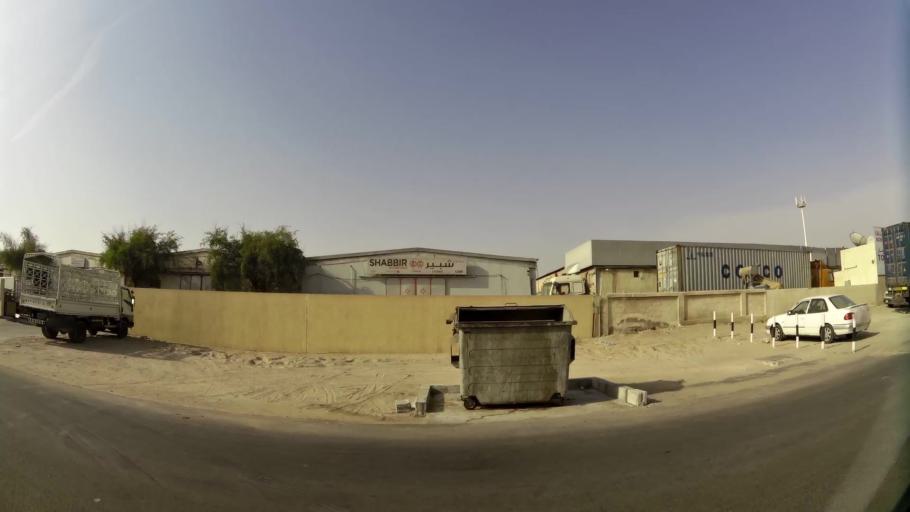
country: AE
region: Ash Shariqah
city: Sharjah
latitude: 25.2291
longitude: 55.3679
